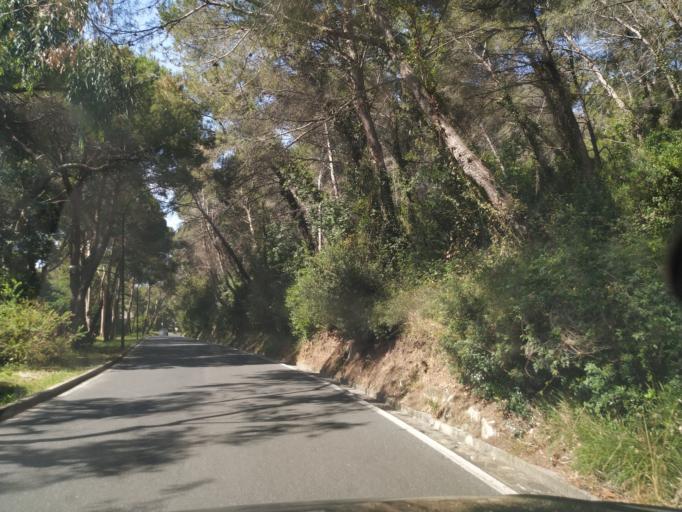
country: IT
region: Liguria
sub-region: Provincia di Savona
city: Marina di Andora
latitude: 43.9562
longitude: 8.1606
